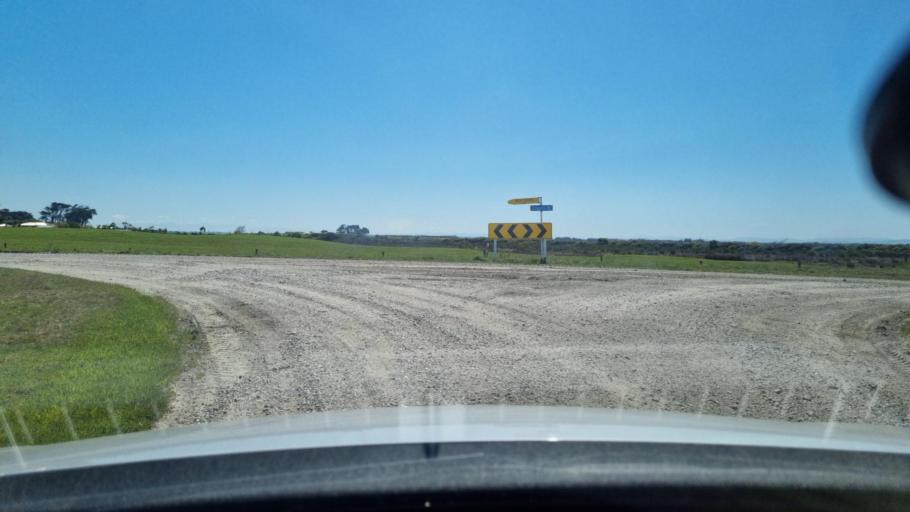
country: NZ
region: Southland
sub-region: Invercargill City
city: Invercargill
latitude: -46.4097
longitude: 168.2633
